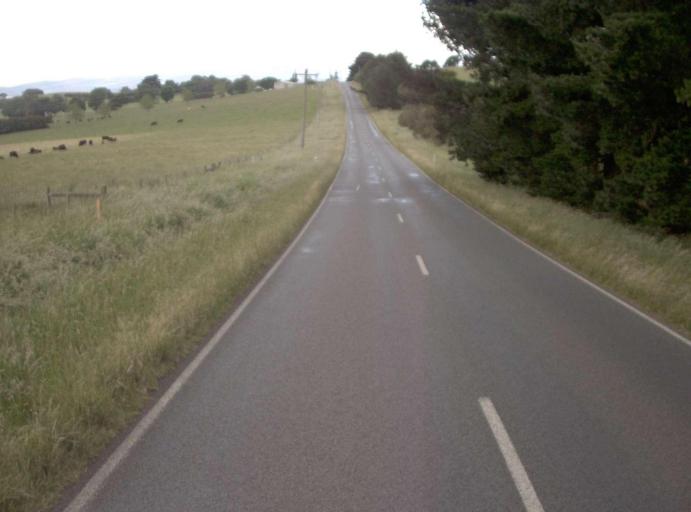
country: AU
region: Victoria
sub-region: Baw Baw
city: Warragul
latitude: -38.1089
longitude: 145.9250
